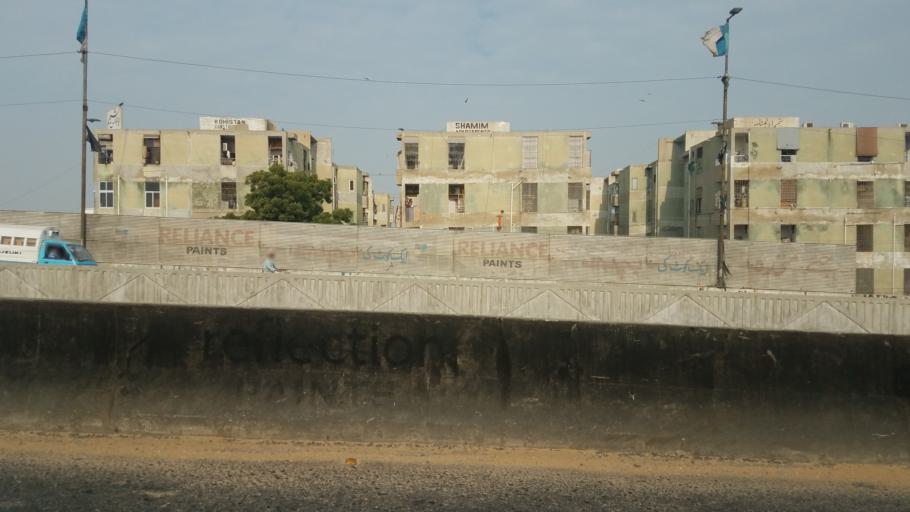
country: PK
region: Sindh
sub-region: Karachi District
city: Karachi
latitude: 24.9281
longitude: 67.0650
